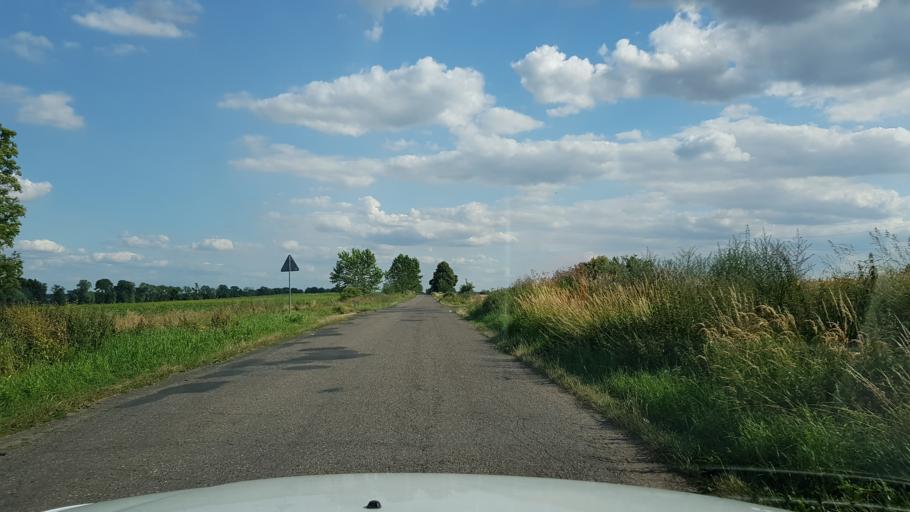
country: PL
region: West Pomeranian Voivodeship
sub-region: Powiat gryfinski
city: Stare Czarnowo
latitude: 53.2939
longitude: 14.8049
